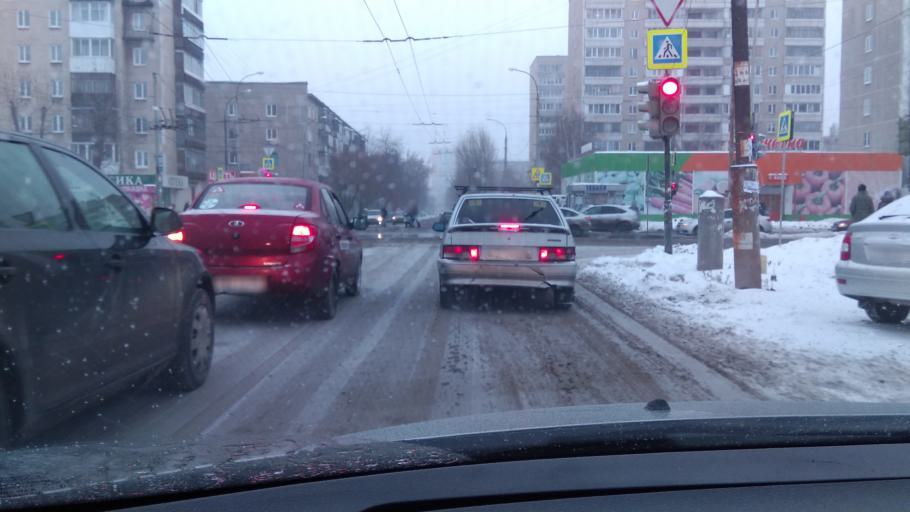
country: RU
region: Sverdlovsk
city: Yekaterinburg
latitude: 56.9095
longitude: 60.5924
